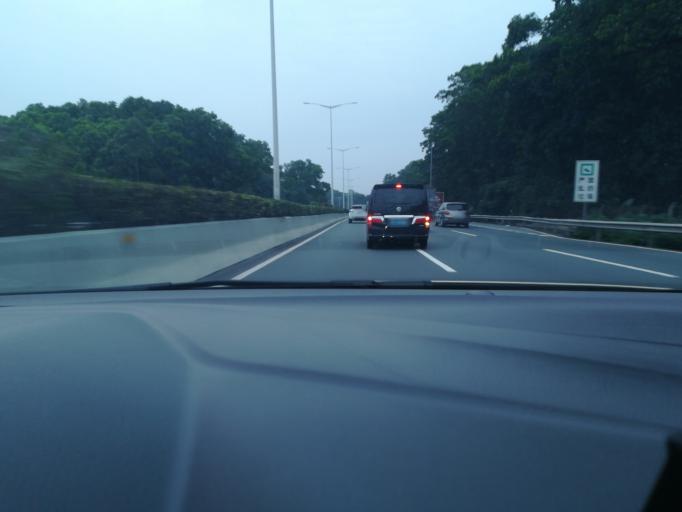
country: CN
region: Guangdong
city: Taihe
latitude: 23.2671
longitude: 113.3610
